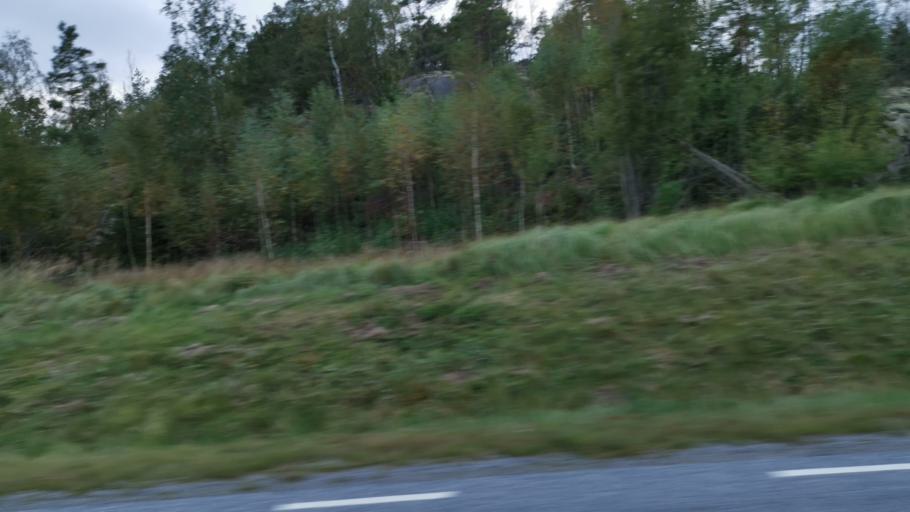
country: SE
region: Vaestra Goetaland
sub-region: Tanums Kommun
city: Tanumshede
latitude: 58.6764
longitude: 11.3406
